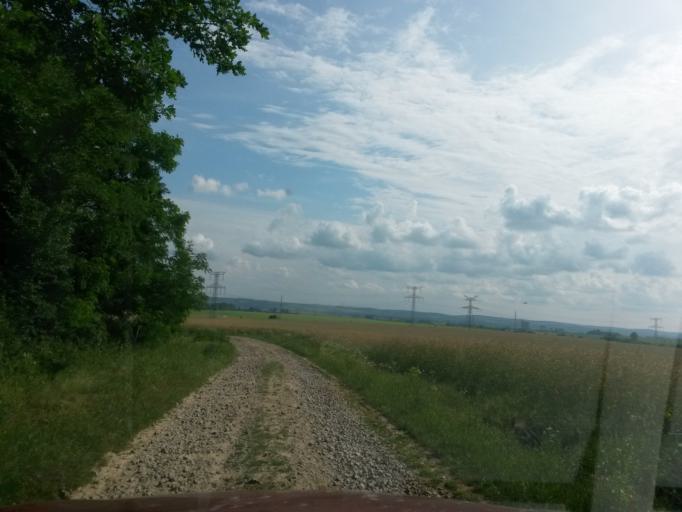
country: SK
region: Kosicky
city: Moldava nad Bodvou
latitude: 48.6103
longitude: 21.1022
